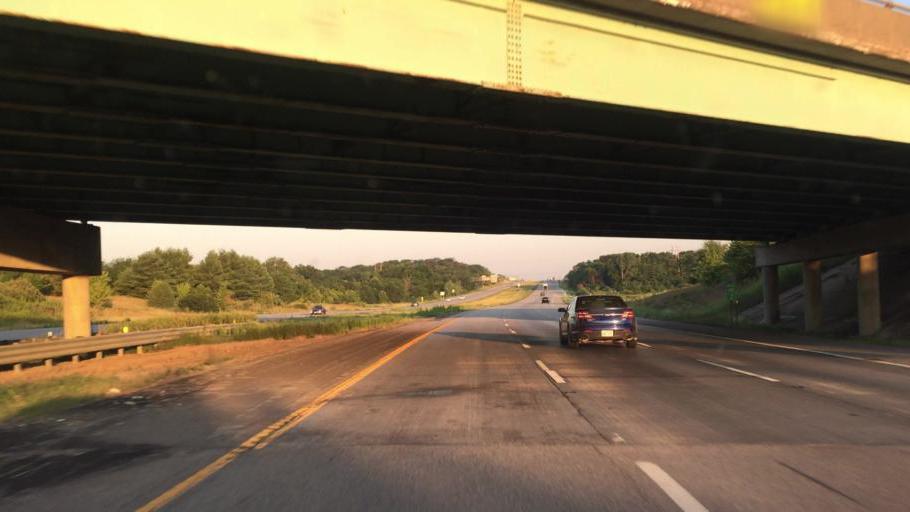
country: US
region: Missouri
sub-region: Clay County
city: Smithville
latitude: 39.3072
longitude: -94.6023
